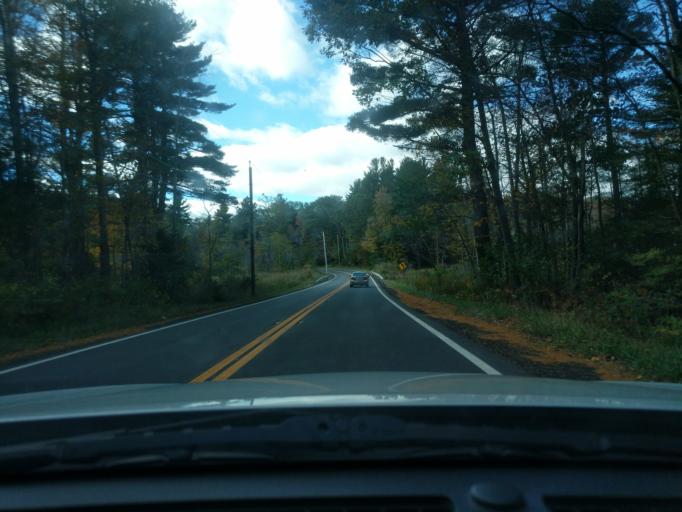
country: US
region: Massachusetts
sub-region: Berkshire County
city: Otis
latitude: 42.1932
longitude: -73.1244
